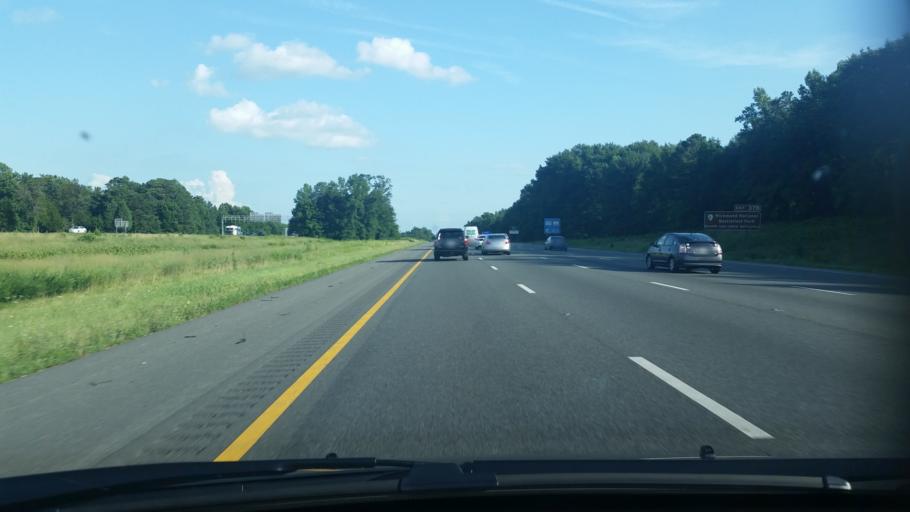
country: US
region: Virginia
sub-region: Hanover County
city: Mechanicsville
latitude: 37.6226
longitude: -77.3681
